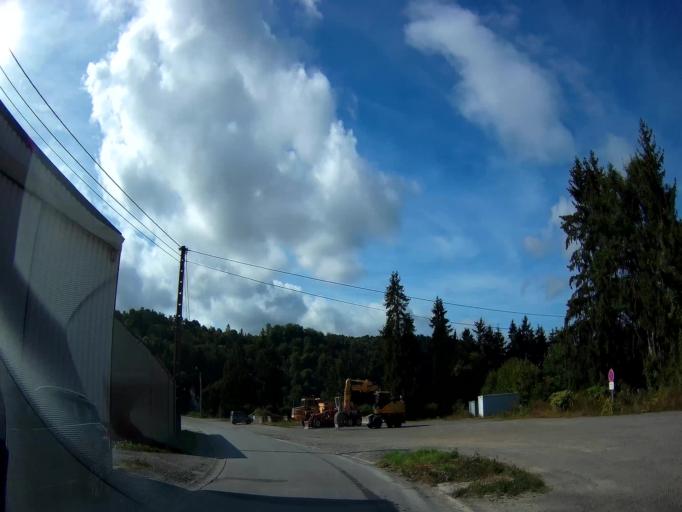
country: BE
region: Wallonia
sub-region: Province de Namur
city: Rochefort
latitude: 50.1568
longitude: 5.2168
